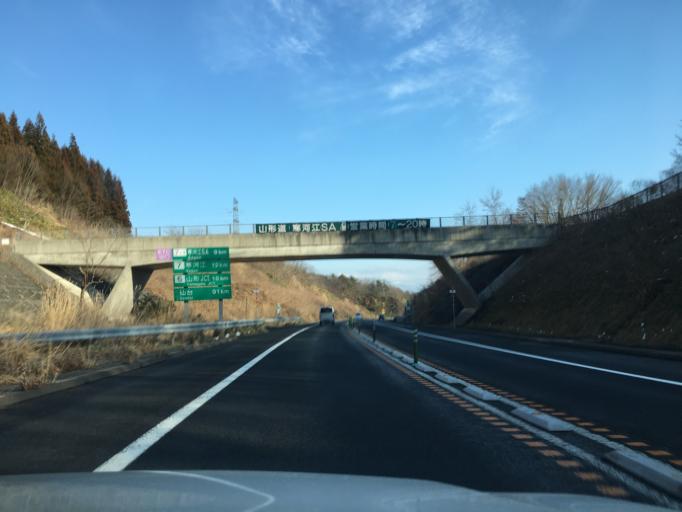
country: JP
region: Yamagata
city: Sagae
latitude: 38.4196
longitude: 140.1840
